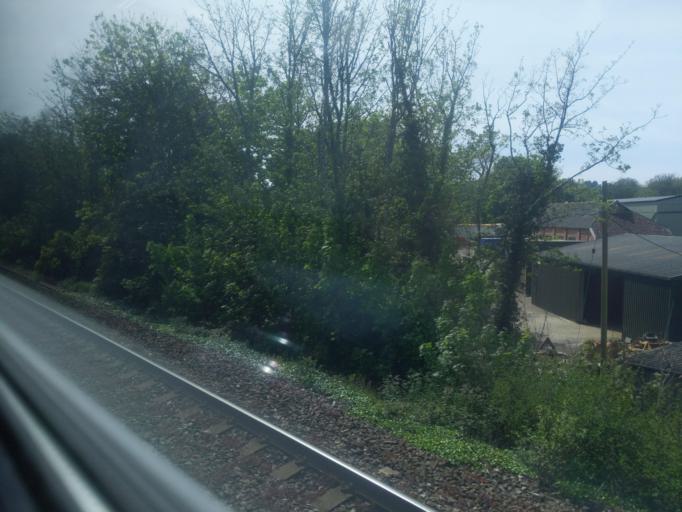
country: GB
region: England
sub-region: Cornwall
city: Hayle
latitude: 50.1668
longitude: -5.4493
